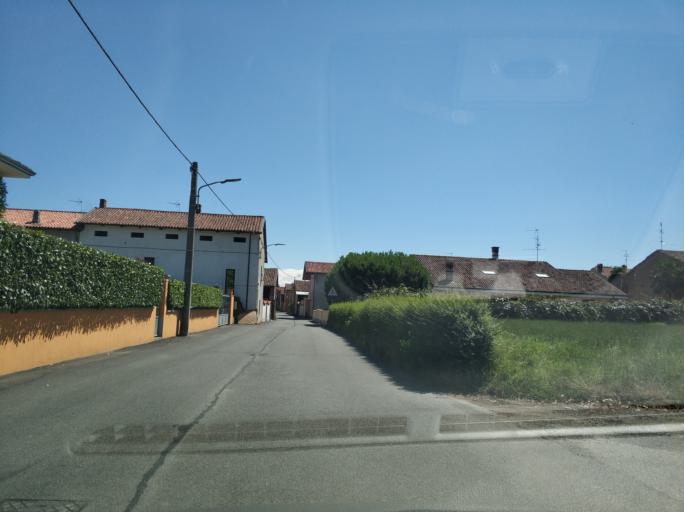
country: IT
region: Piedmont
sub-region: Provincia di Vercelli
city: Cigliano
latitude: 45.3110
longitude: 8.0158
